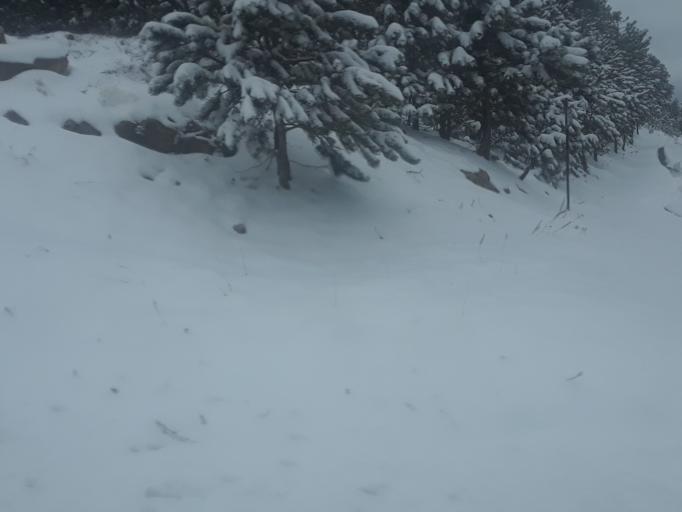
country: US
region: Colorado
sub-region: Boulder County
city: Coal Creek
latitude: 39.9205
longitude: -105.3701
